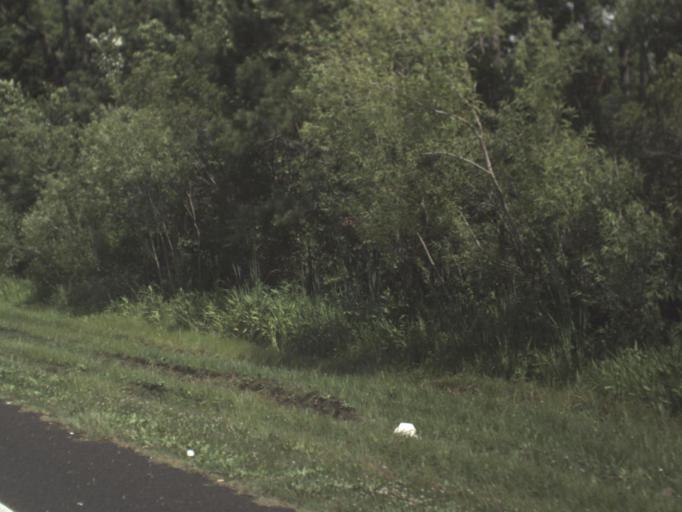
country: US
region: Florida
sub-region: Nassau County
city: Yulee
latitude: 30.6291
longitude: -81.5622
